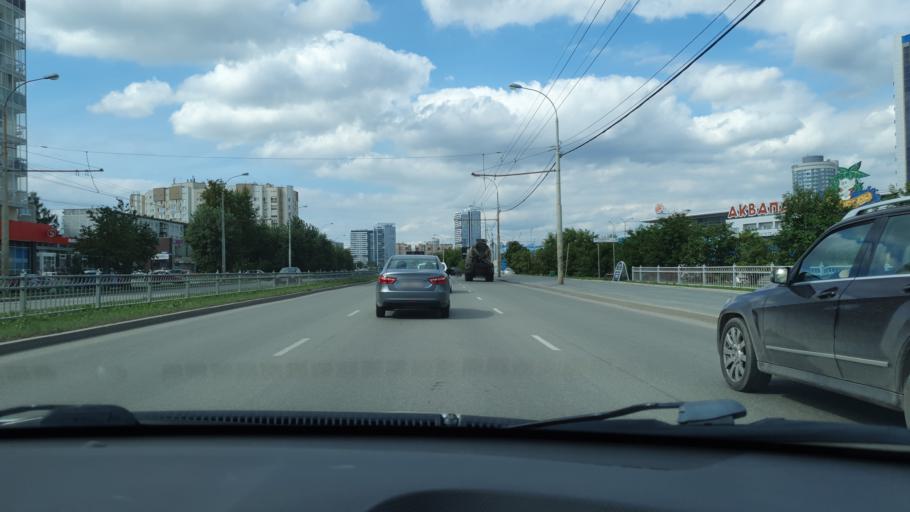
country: RU
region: Sverdlovsk
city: Yekaterinburg
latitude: 56.7889
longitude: 60.6466
